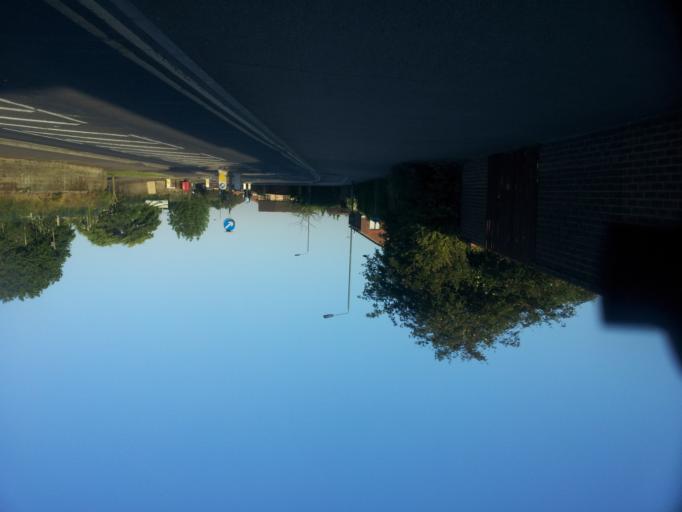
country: GB
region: England
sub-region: Greater London
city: Belvedere
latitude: 51.4905
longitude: 0.1324
